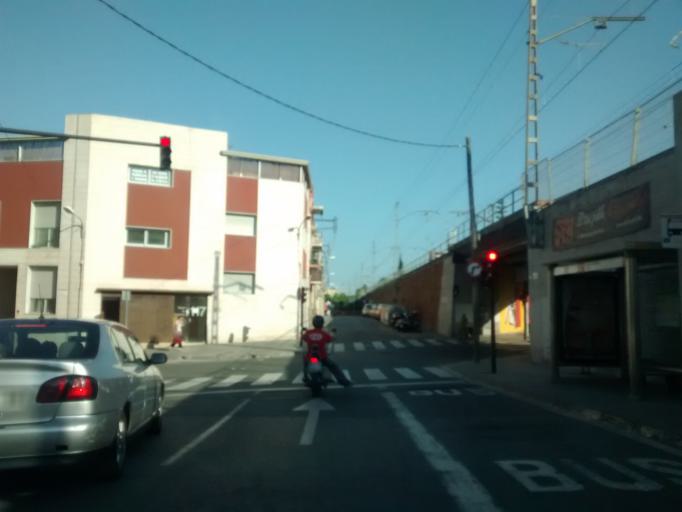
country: ES
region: Catalonia
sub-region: Provincia de Barcelona
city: Sant Vicenc dels Horts
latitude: 41.3912
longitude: 2.0099
